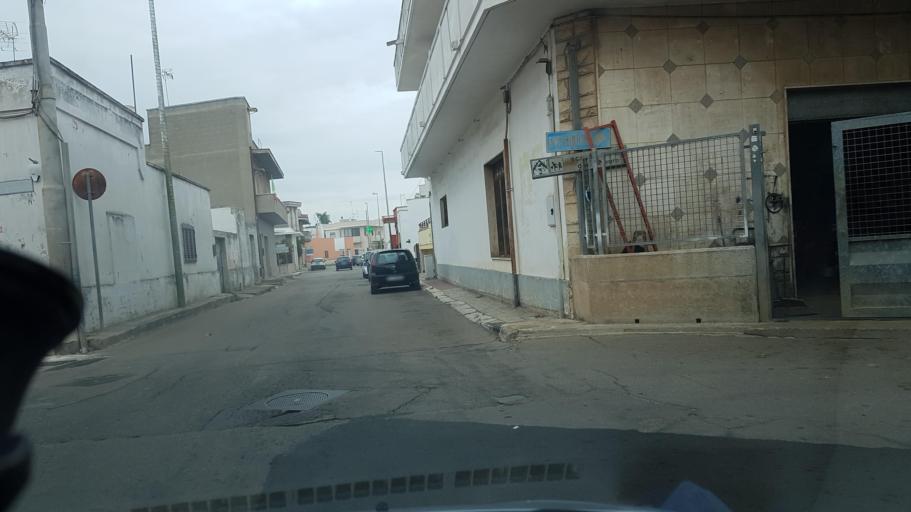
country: IT
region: Apulia
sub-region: Provincia di Lecce
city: Veglie
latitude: 40.3399
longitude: 17.9676
